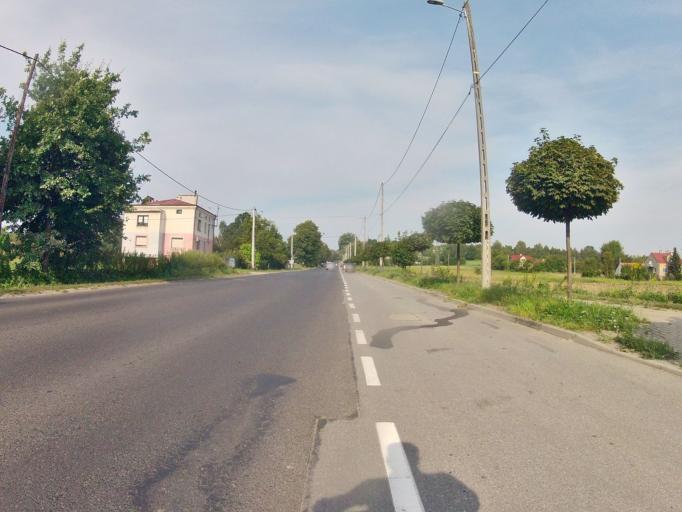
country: PL
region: Subcarpathian Voivodeship
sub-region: Powiat jasielski
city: Jaslo
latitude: 49.7530
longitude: 21.4540
